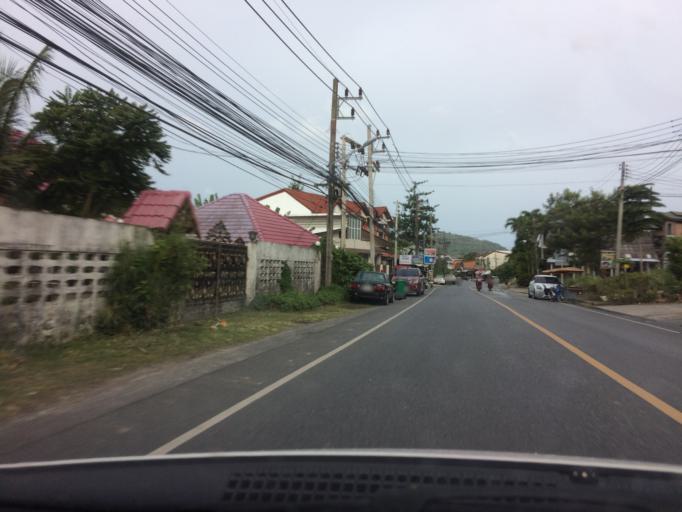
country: TH
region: Phuket
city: Ban Ratsada
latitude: 7.9055
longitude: 98.4075
